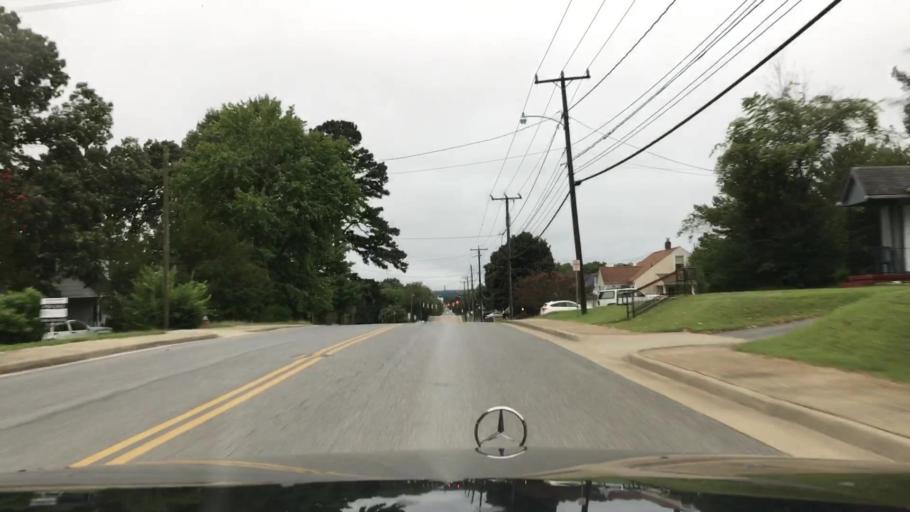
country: US
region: Virginia
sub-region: Campbell County
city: Altavista
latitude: 37.1182
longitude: -79.2786
